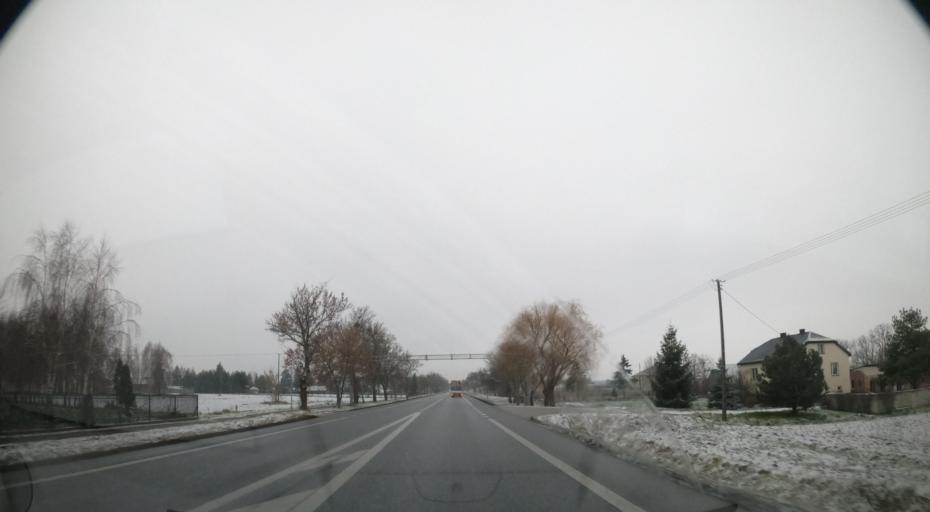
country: PL
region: Masovian Voivodeship
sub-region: Powiat warszawski zachodni
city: Bieniewice
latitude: 52.2005
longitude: 20.5703
